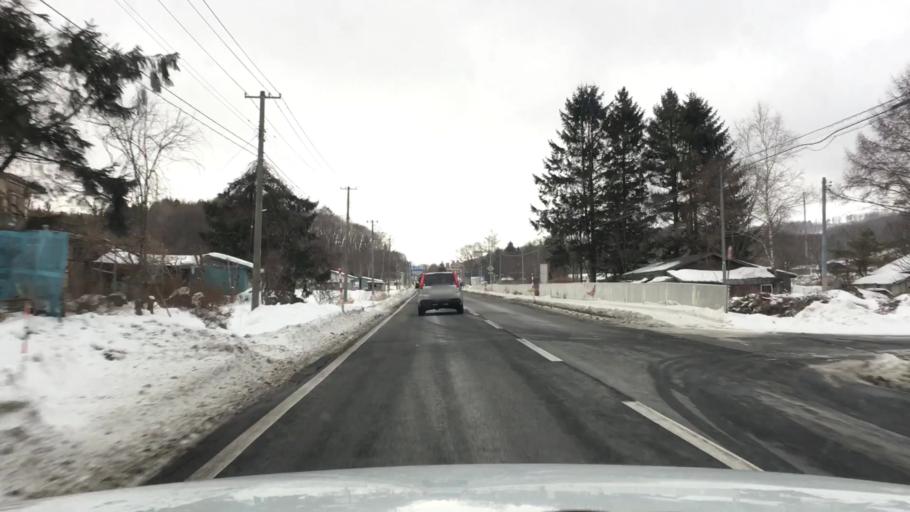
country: JP
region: Iwate
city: Morioka-shi
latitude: 39.6487
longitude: 141.3568
